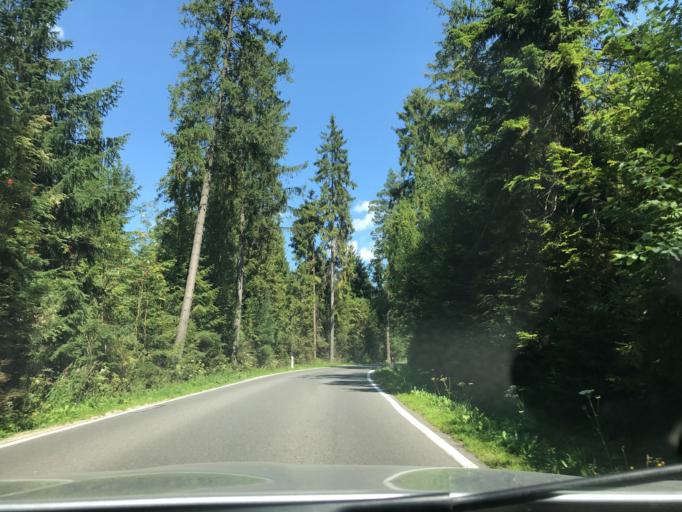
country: PL
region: Lesser Poland Voivodeship
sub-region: Powiat nowotarski
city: Klikuszowa
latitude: 49.5252
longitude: 19.9618
